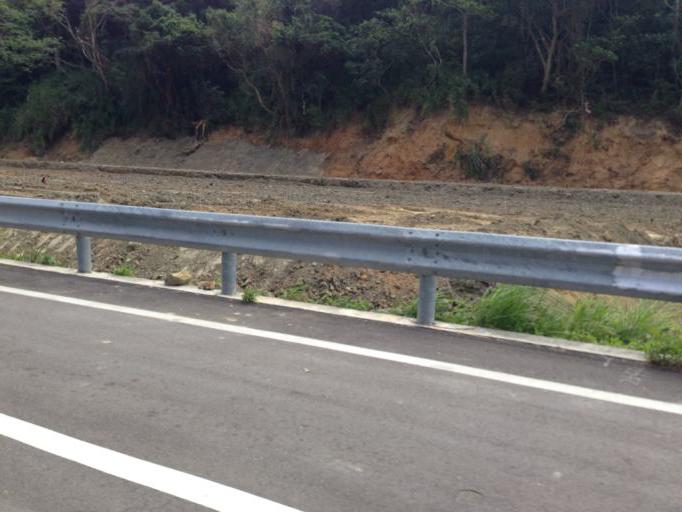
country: TW
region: Taiwan
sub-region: Hsinchu
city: Hsinchu
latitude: 24.7475
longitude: 120.9648
